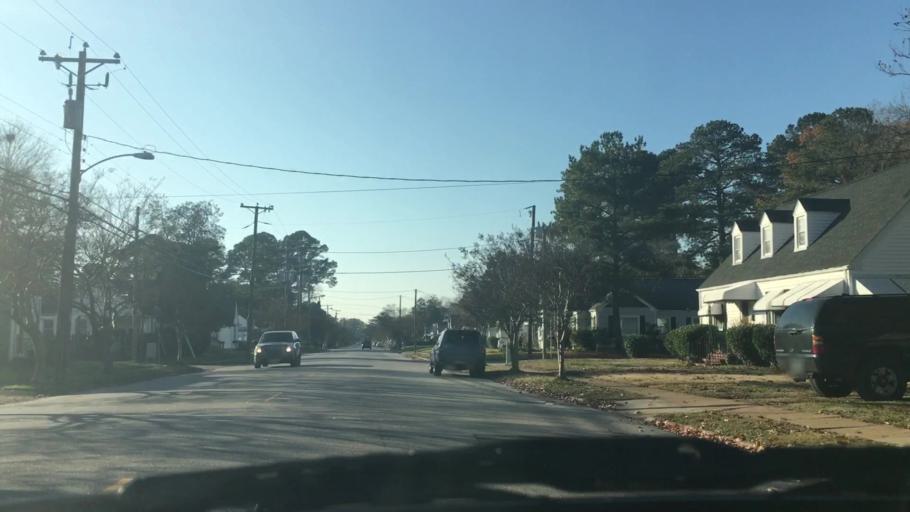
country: US
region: Virginia
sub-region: City of Norfolk
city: Norfolk
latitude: 36.8900
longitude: -76.2436
